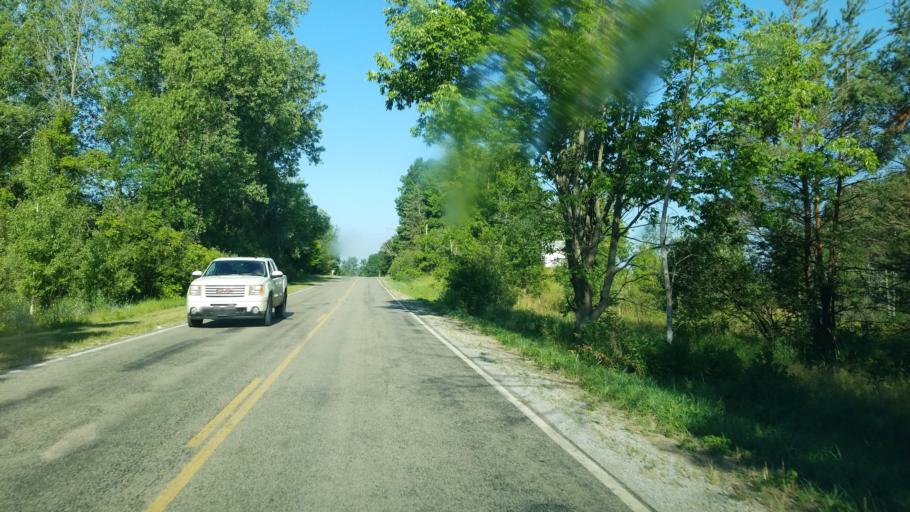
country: US
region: Michigan
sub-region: Montcalm County
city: Howard City
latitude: 43.4904
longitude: -85.4191
